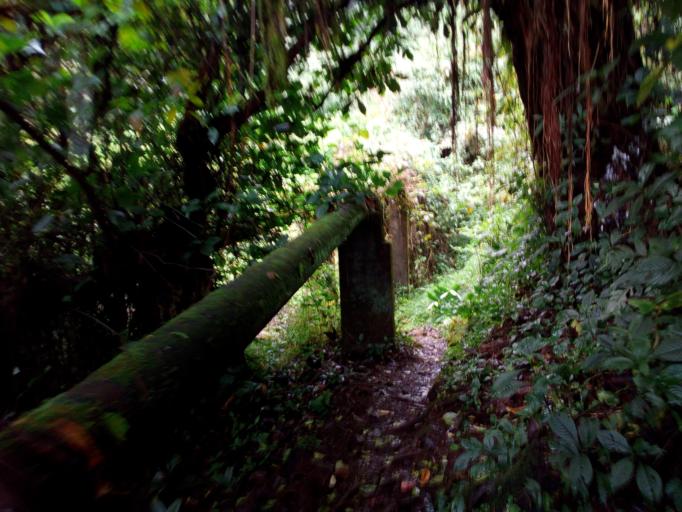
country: CM
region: South-West Province
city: Buea
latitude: 4.1625
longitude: 9.2238
